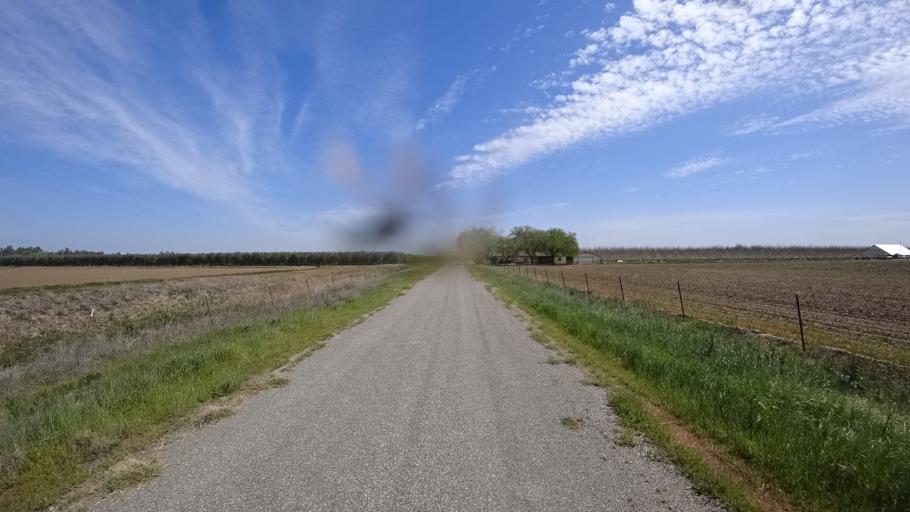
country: US
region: California
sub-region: Glenn County
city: Willows
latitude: 39.5769
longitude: -122.1997
